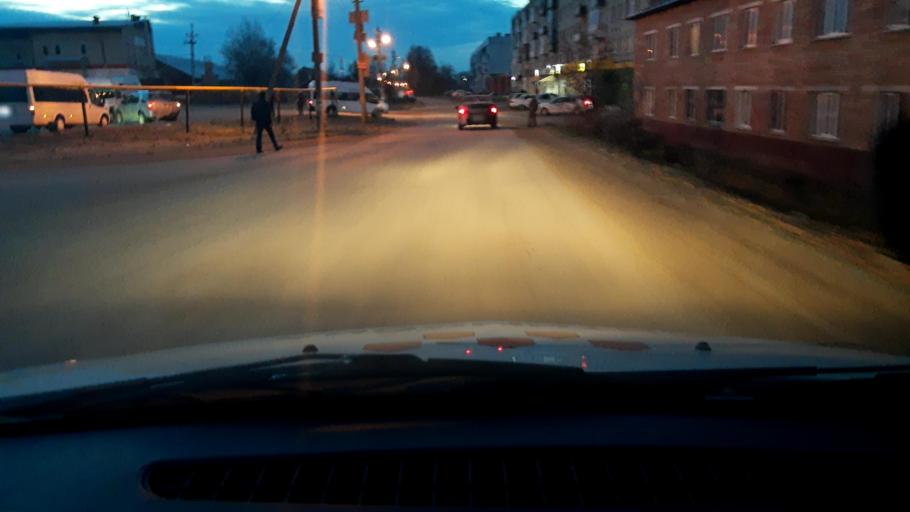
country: RU
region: Bashkortostan
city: Iglino
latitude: 54.7786
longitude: 56.2224
